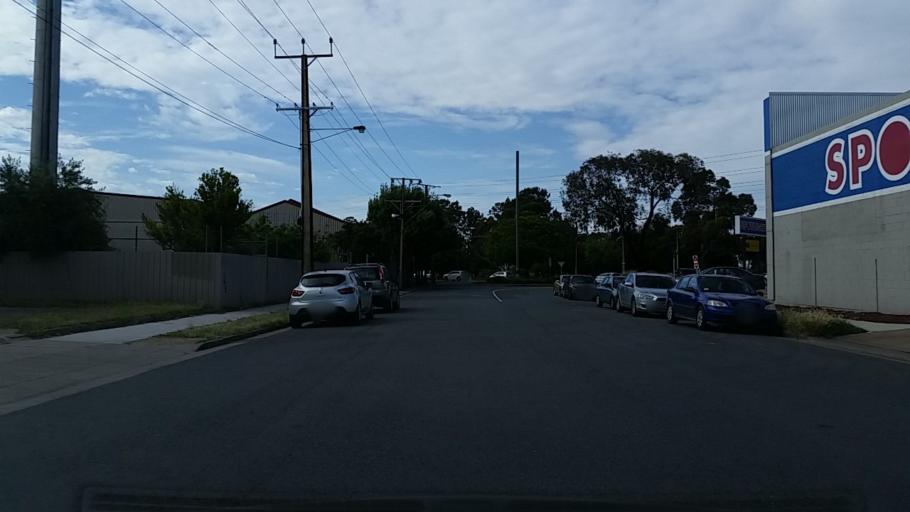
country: AU
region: South Australia
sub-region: Charles Sturt
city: Albert Park
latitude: -34.8754
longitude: 138.5253
